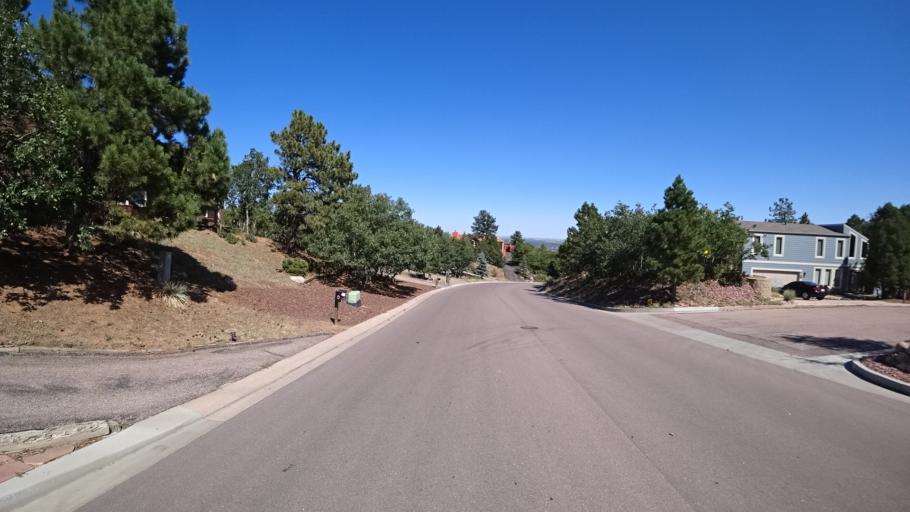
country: US
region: Colorado
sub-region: El Paso County
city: Colorado Springs
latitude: 38.8227
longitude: -104.8723
